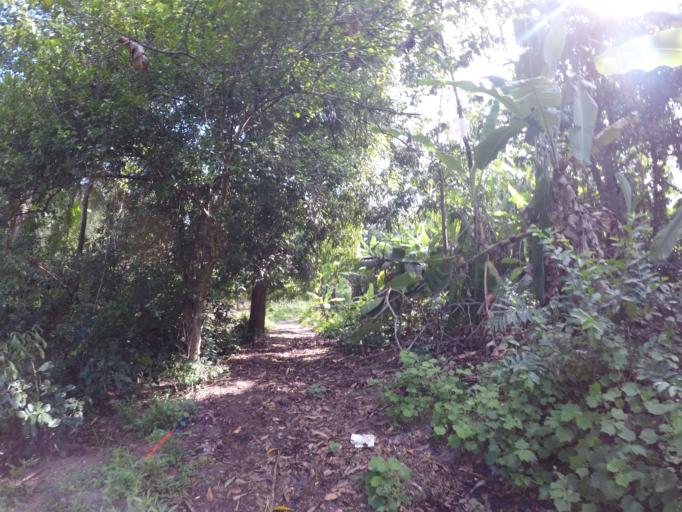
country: TZ
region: Pemba South
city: Mtambile
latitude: -5.3817
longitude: 39.7185
